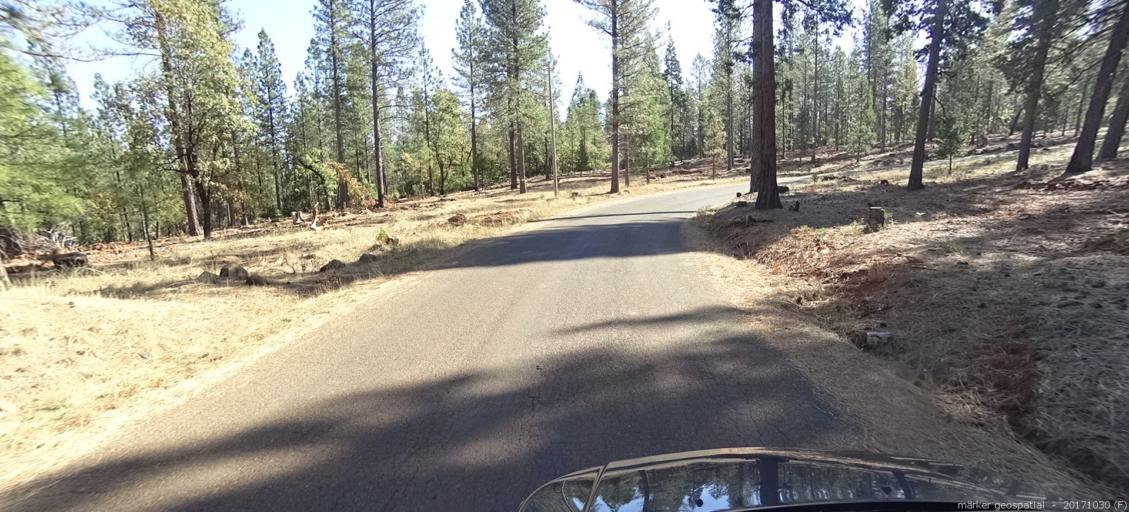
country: US
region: California
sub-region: Shasta County
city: Shingletown
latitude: 40.6215
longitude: -121.8929
